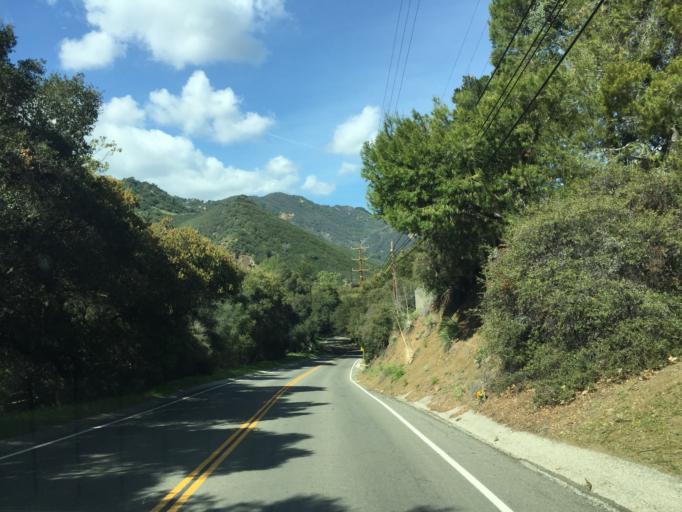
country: US
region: California
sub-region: Los Angeles County
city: Malibu Beach
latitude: 34.0786
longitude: -118.6972
